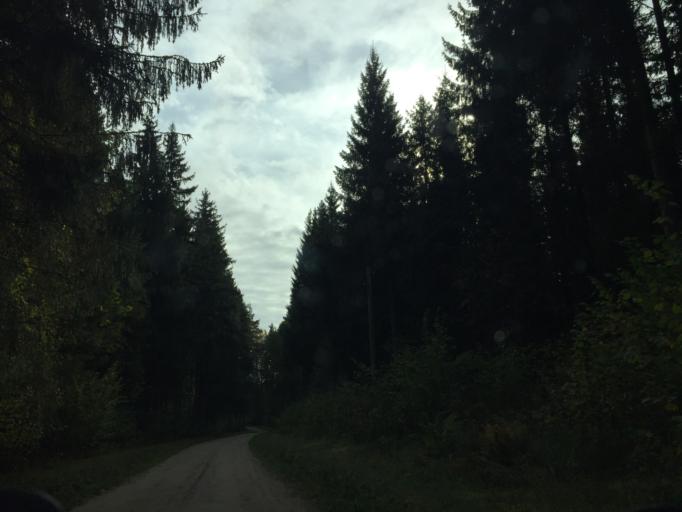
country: LV
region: Jaunpils
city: Jaunpils
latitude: 56.5814
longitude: 23.0249
